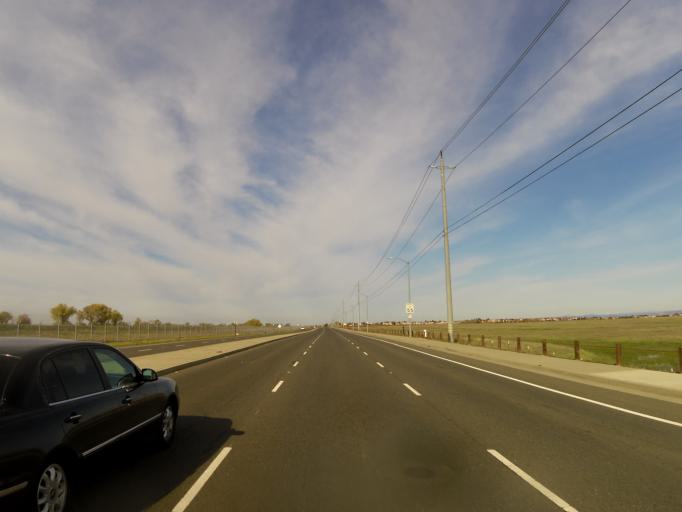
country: US
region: California
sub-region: Sacramento County
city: Rancho Cordova
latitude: 38.5267
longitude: -121.2428
